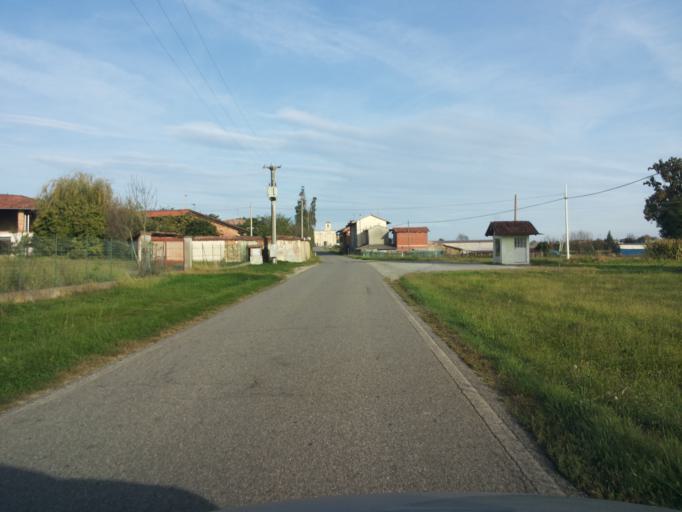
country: IT
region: Piedmont
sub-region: Provincia di Biella
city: Salussola
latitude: 45.4458
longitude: 8.1455
